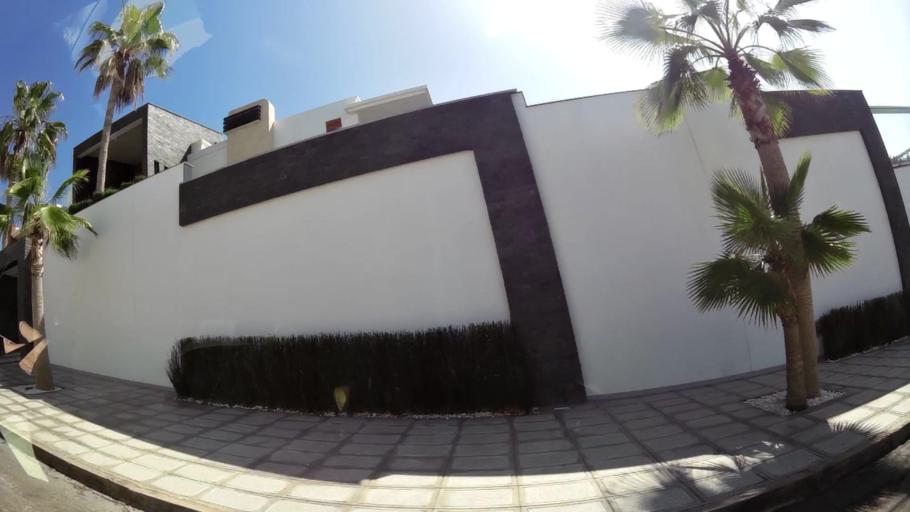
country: MA
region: Souss-Massa-Draa
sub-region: Agadir-Ida-ou-Tnan
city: Agadir
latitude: 30.4416
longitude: -9.5940
